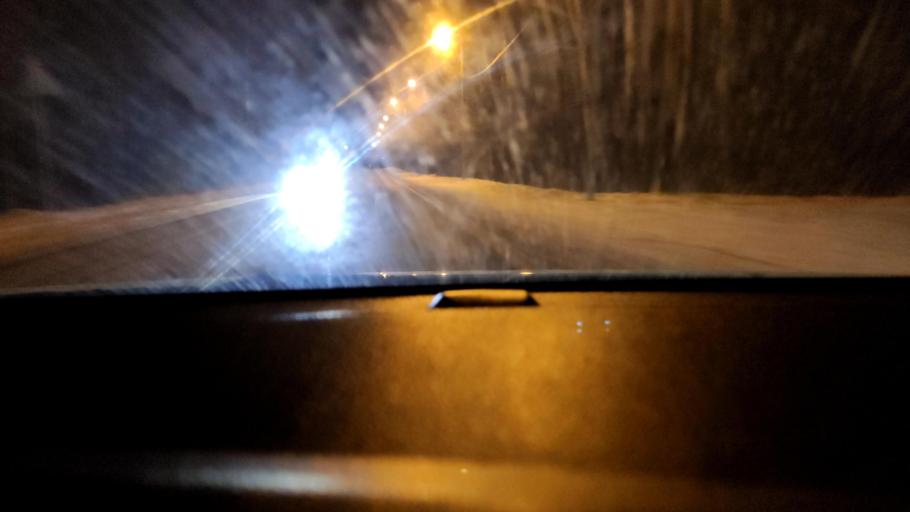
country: RU
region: Tatarstan
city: Osinovo
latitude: 55.8432
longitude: 48.8919
